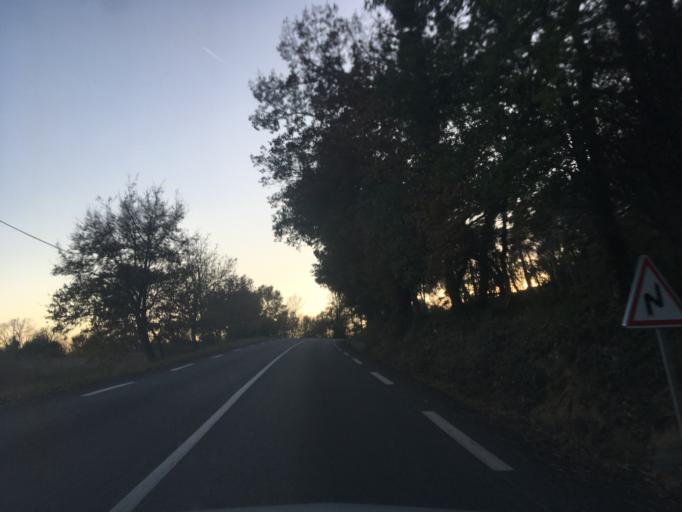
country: FR
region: Provence-Alpes-Cote d'Azur
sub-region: Departement des Alpes-Maritimes
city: Le Tignet
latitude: 43.6104
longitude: 6.8144
